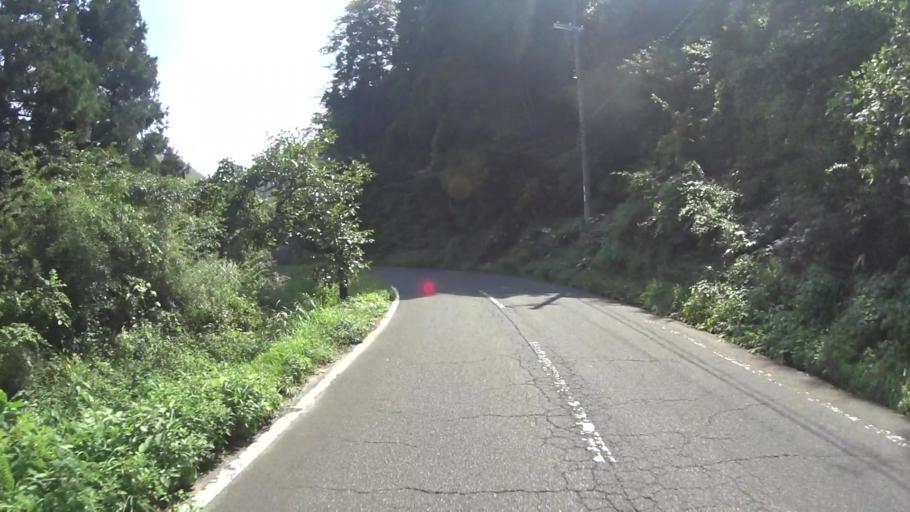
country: JP
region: Kyoto
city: Miyazu
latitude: 35.6876
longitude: 135.1569
